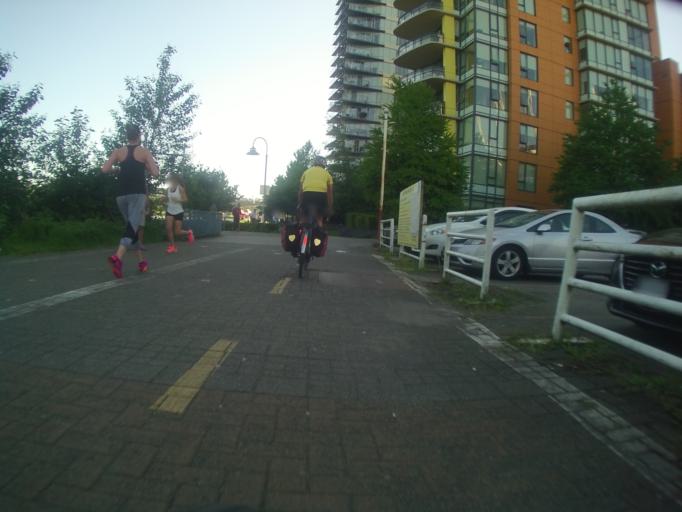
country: CA
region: British Columbia
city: West End
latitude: 49.2743
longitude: -123.1110
